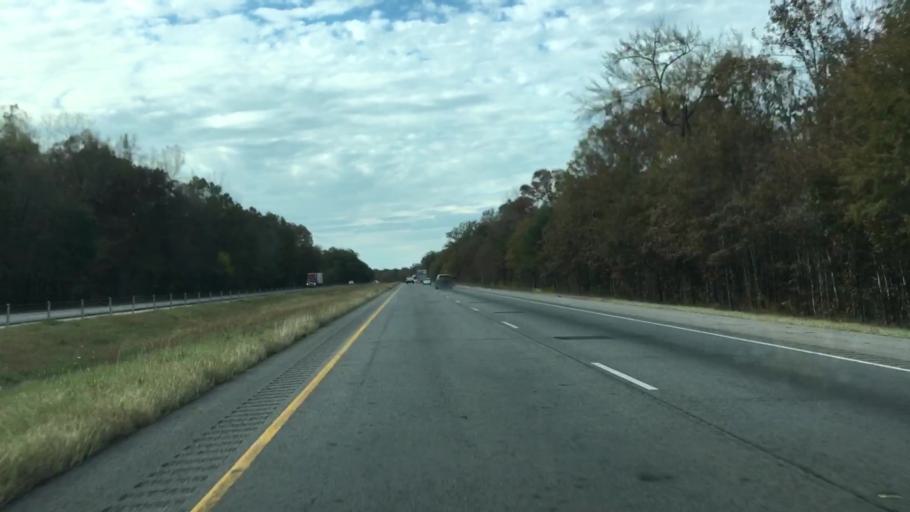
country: US
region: Arkansas
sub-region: Pope County
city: Atkins
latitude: 35.2384
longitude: -92.8555
